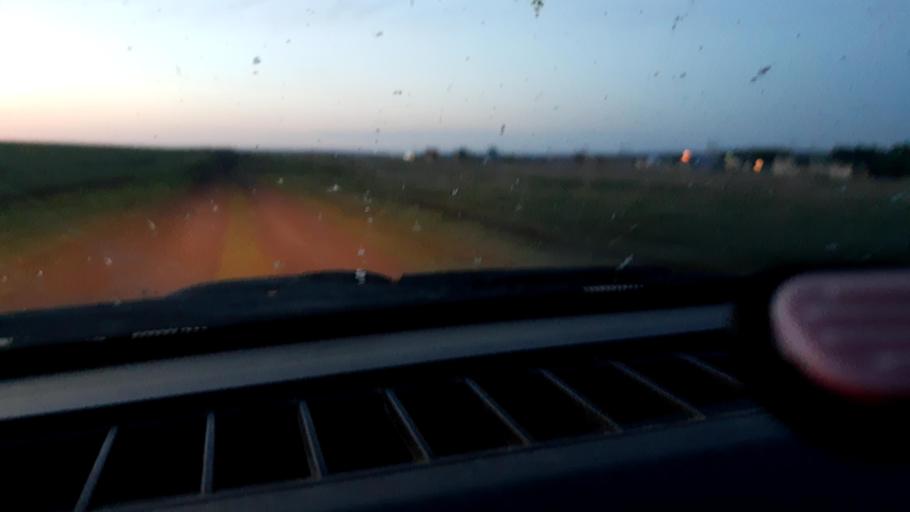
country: RU
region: Bashkortostan
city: Asanovo
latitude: 54.8546
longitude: 55.5844
